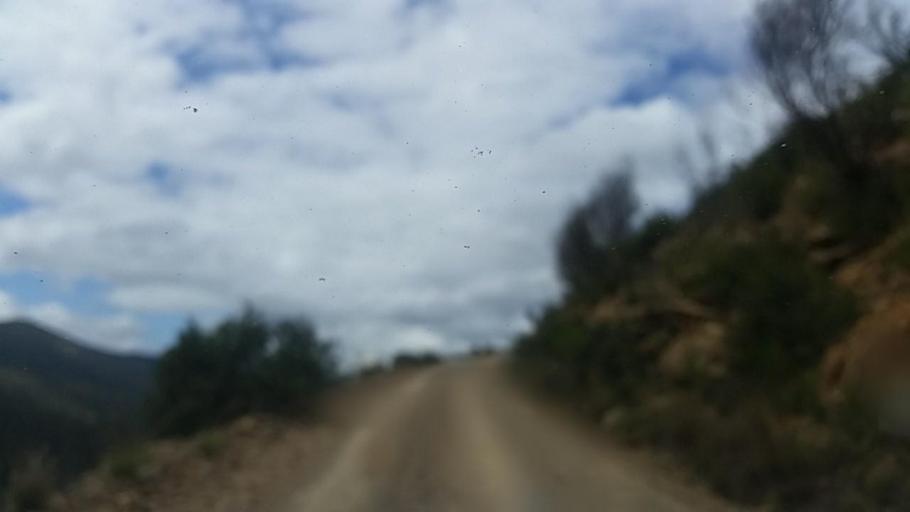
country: ZA
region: Western Cape
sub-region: Eden District Municipality
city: Knysna
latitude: -33.8218
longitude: 23.1781
